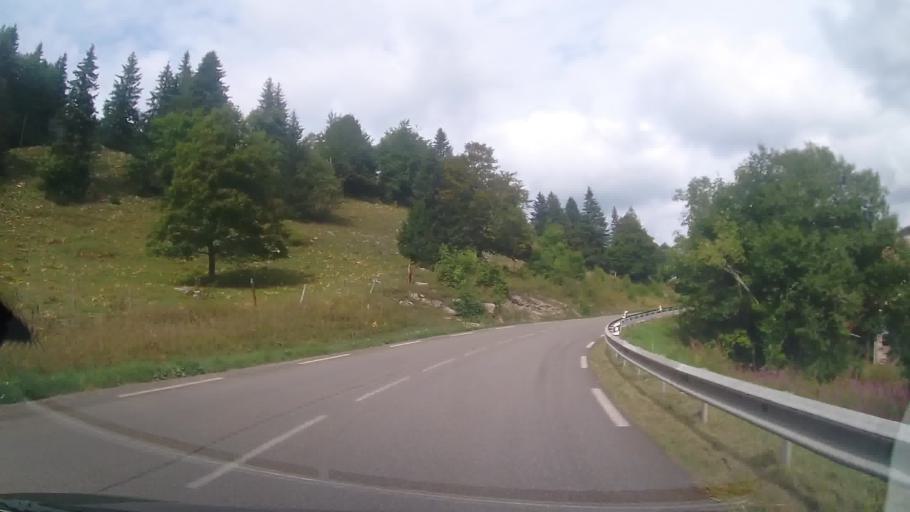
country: FR
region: Franche-Comte
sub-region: Departement du Jura
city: Les Rousses
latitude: 46.4328
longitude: 6.0737
